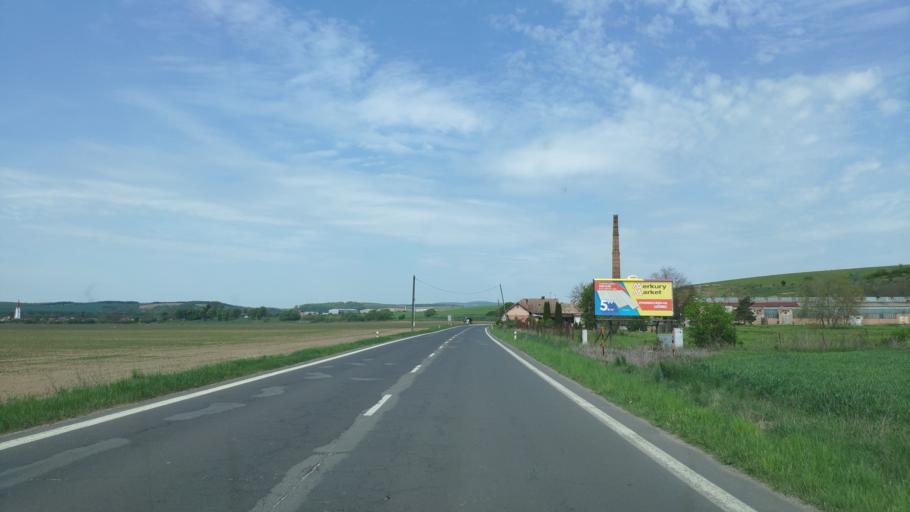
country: HU
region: Borsod-Abauj-Zemplen
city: Putnok
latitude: 48.4252
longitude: 20.3097
